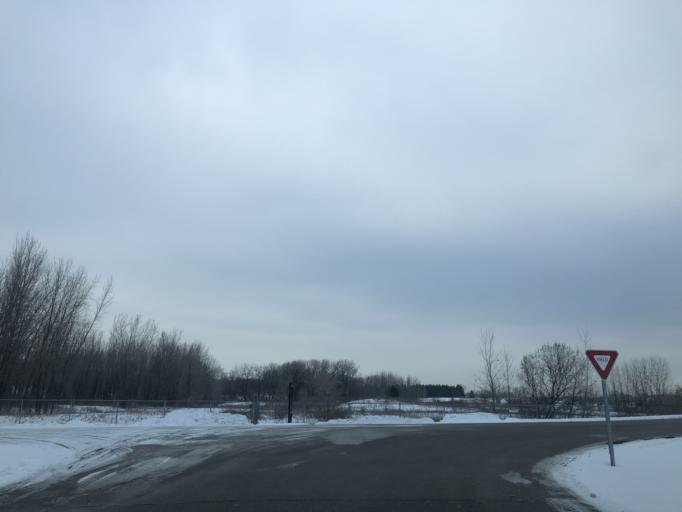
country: US
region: Minnesota
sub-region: Ramsey County
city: Shoreview
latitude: 45.0830
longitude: -93.1639
